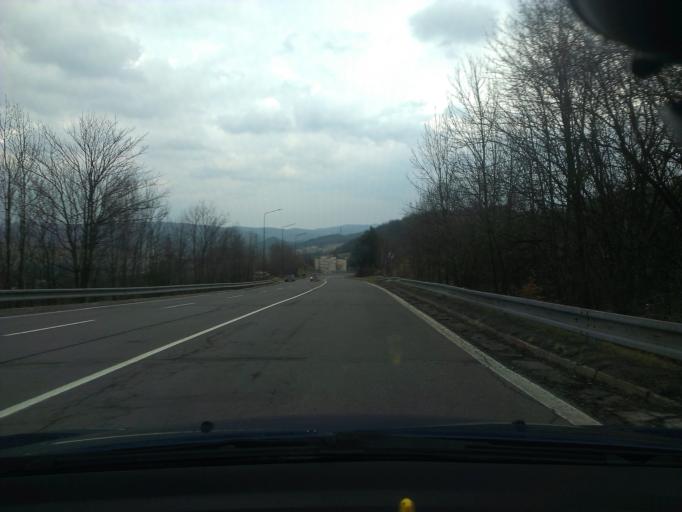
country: SK
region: Banskobystricky
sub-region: Okres Banska Bystrica
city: Banska Stiavnica
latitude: 48.4515
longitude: 18.9021
